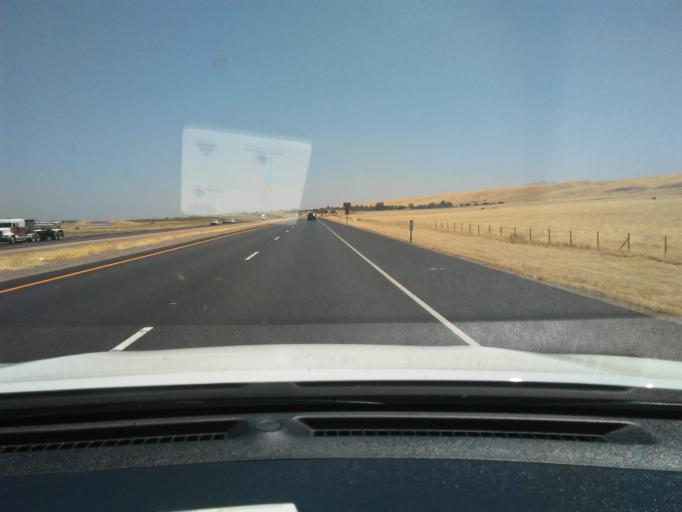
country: US
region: California
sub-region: San Joaquin County
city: Tracy
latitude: 37.6494
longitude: -121.4199
